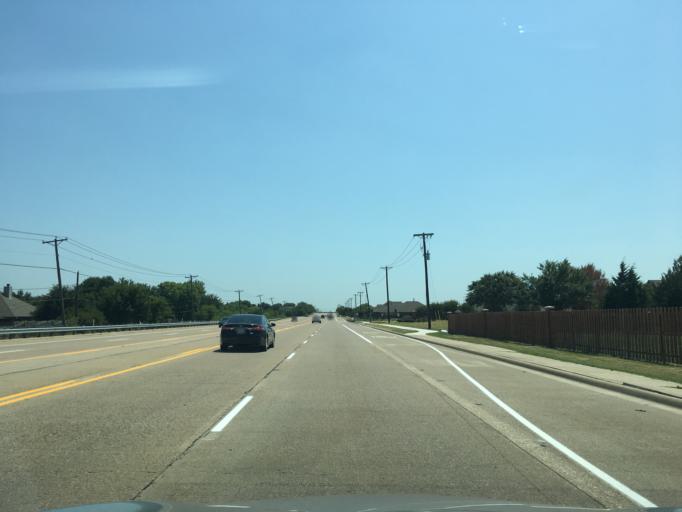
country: US
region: Texas
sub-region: Tarrant County
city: Edgecliff Village
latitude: 32.6292
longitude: -97.3487
